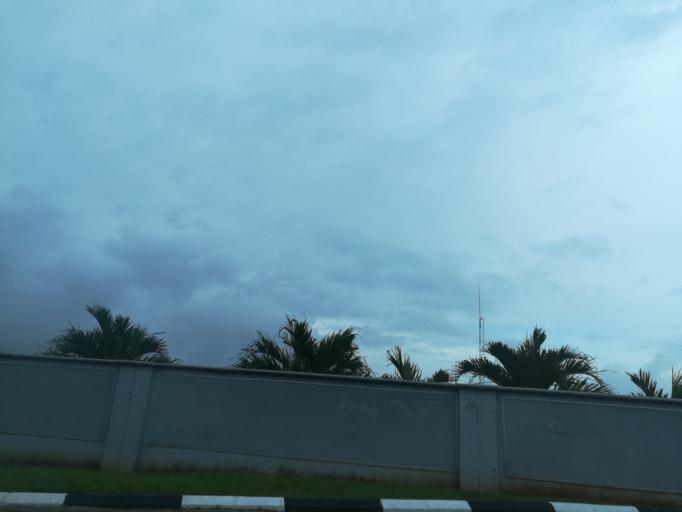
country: NG
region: Lagos
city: Ikeja
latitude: 6.5835
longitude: 3.3334
